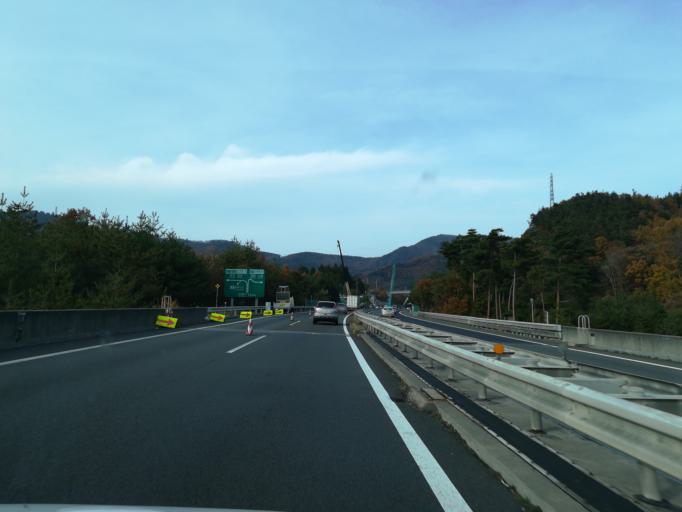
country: JP
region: Nagano
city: Ueda
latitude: 36.4624
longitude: 138.1982
